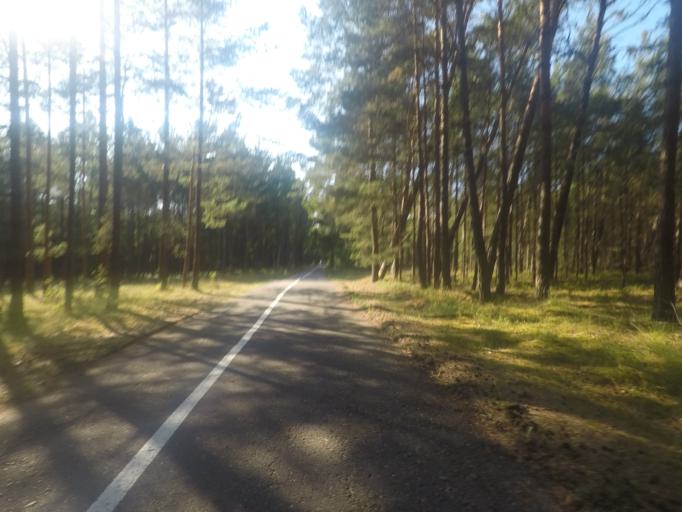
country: LT
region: Klaipedos apskritis
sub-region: Klaipeda
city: Klaipeda
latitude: 55.5484
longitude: 21.1043
